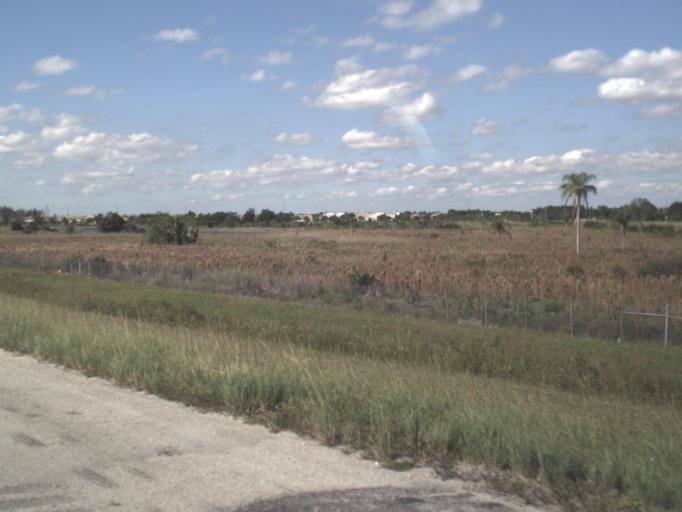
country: US
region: Florida
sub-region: Miami-Dade County
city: Country Club
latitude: 25.9633
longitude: -80.3338
